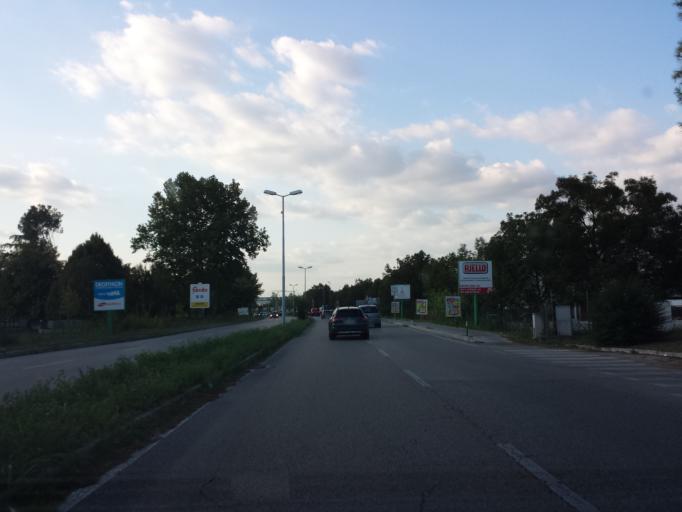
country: IT
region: Veneto
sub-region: Provincia di Padova
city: Mejaniga
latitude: 45.4331
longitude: 11.8979
